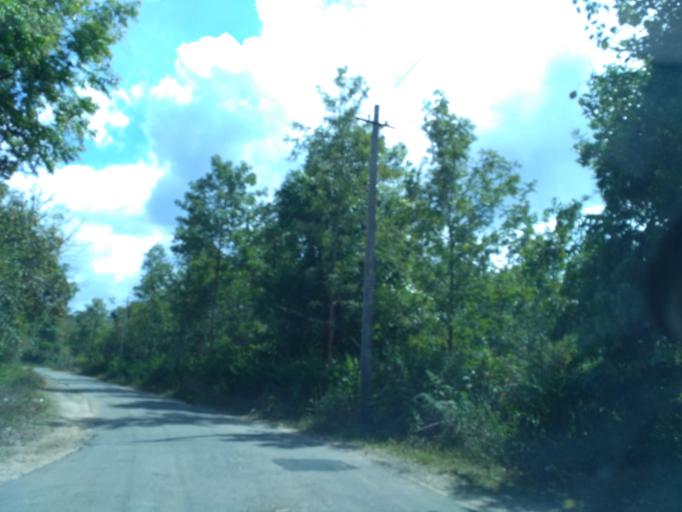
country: IN
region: Karnataka
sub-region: Kodagu
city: Madikeri
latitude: 12.4101
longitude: 75.7123
